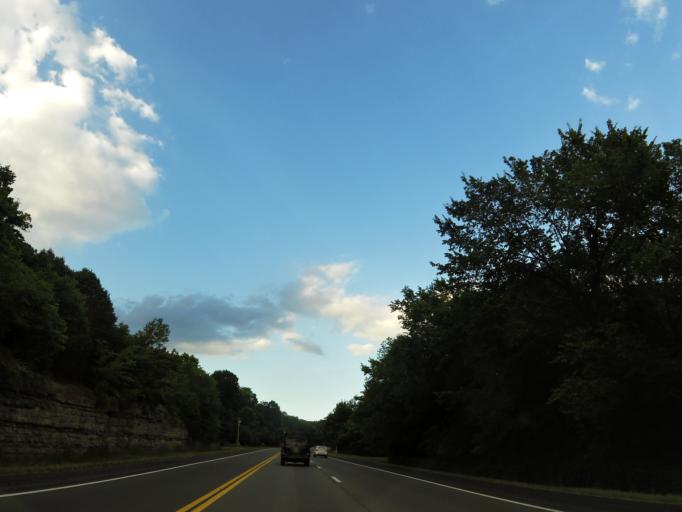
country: US
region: Tennessee
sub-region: Maury County
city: Columbia
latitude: 35.6360
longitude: -86.9308
